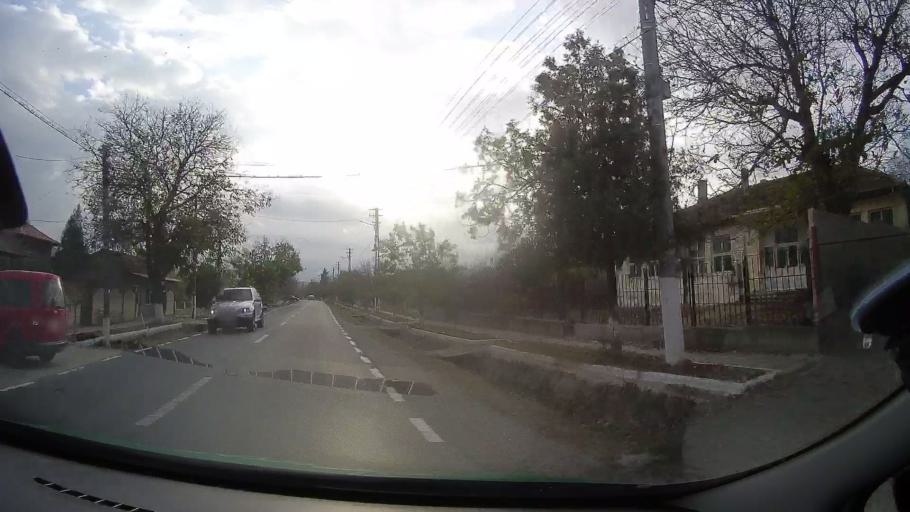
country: RO
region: Constanta
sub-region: Comuna Mircea Voda
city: Mircea Voda
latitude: 44.2798
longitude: 28.1752
